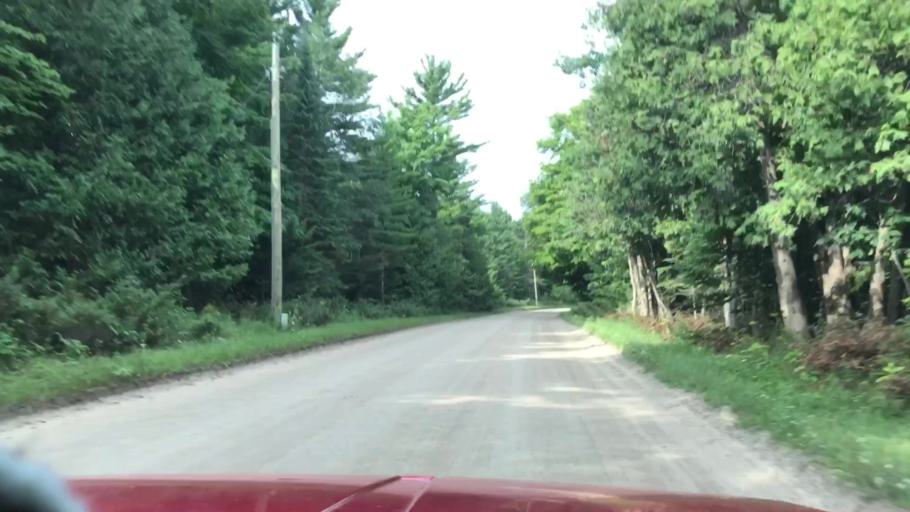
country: US
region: Michigan
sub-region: Charlevoix County
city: Charlevoix
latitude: 45.7281
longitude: -85.5322
